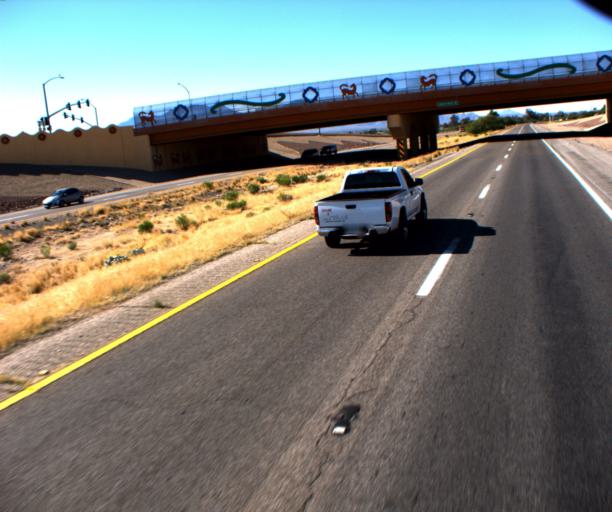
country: US
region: Arizona
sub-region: Pima County
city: Green Valley
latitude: 31.9068
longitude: -110.9858
